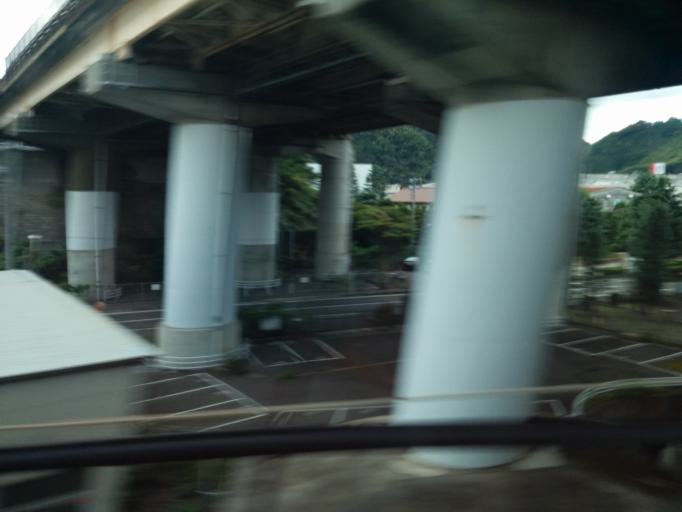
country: JP
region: Shizuoka
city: Shizuoka-shi
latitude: 34.9286
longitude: 138.3623
